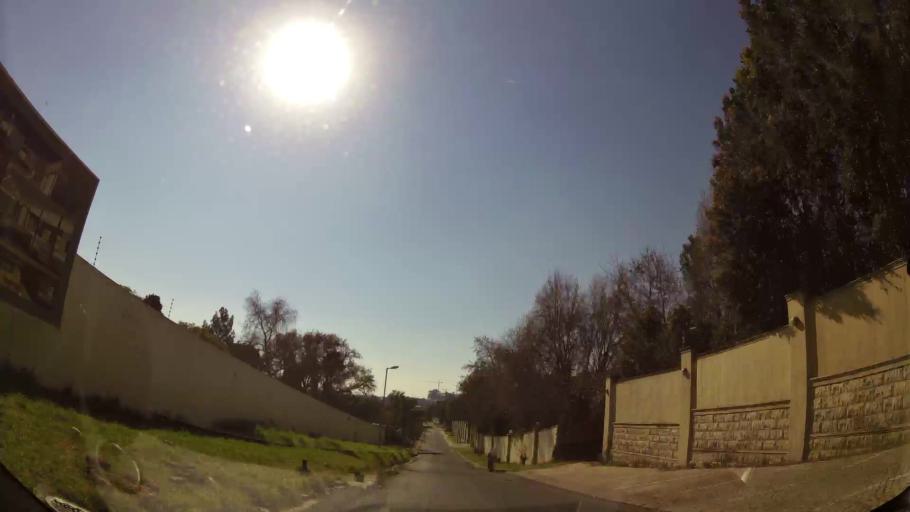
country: ZA
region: Gauteng
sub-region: City of Johannesburg Metropolitan Municipality
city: Johannesburg
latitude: -26.1098
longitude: 28.0421
